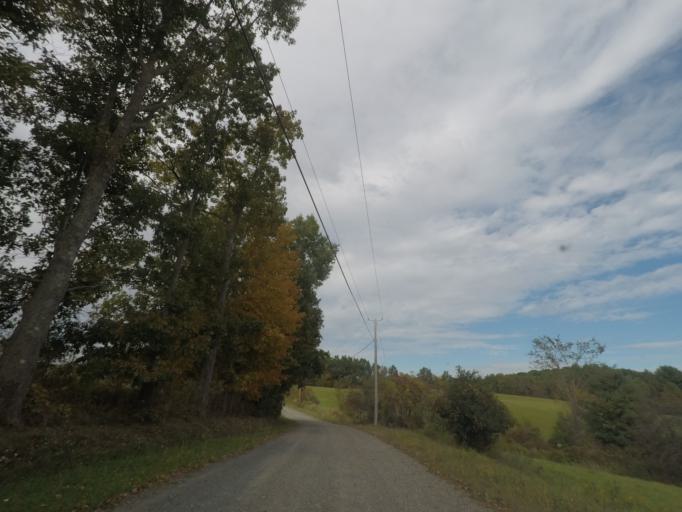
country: US
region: New York
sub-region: Rensselaer County
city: Nassau
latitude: 42.5793
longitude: -73.6130
